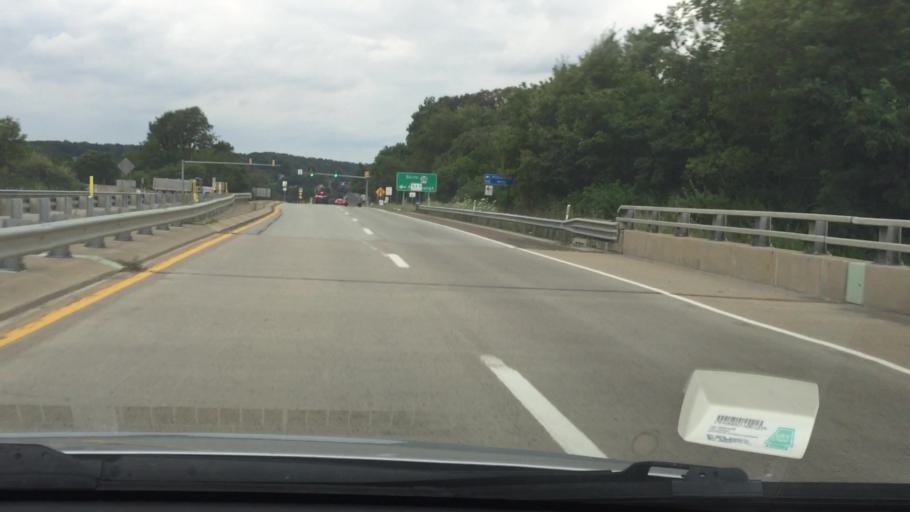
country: US
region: Pennsylvania
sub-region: Armstrong County
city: Freeport
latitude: 40.6911
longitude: -79.7100
